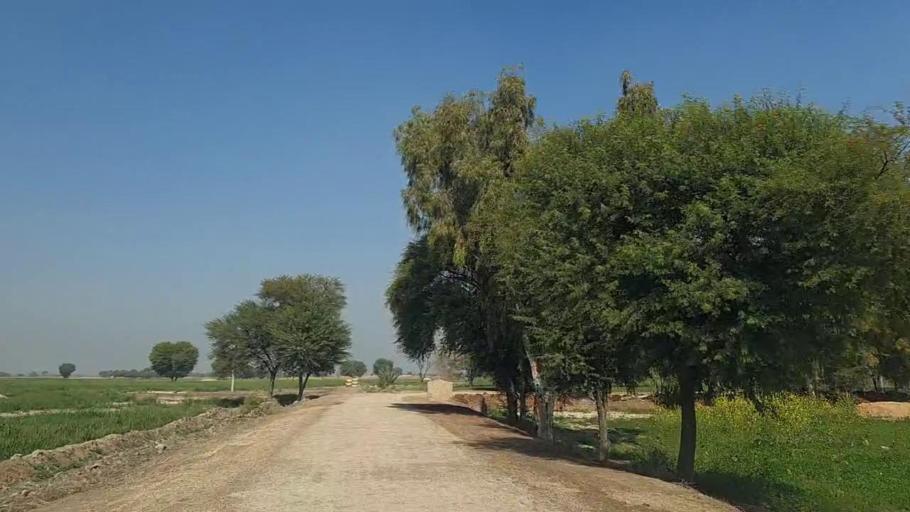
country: PK
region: Sindh
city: Shahpur Chakar
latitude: 26.2018
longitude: 68.5543
